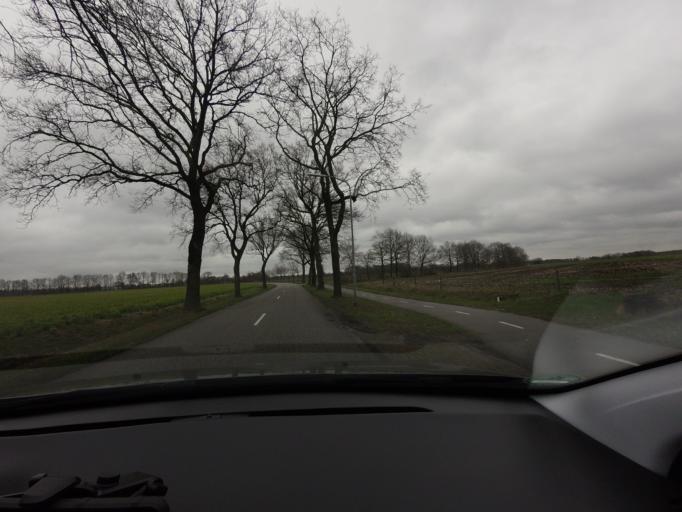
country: NL
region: Drenthe
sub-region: Gemeente Hoogeveen
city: Hoogeveen
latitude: 52.8355
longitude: 6.5308
